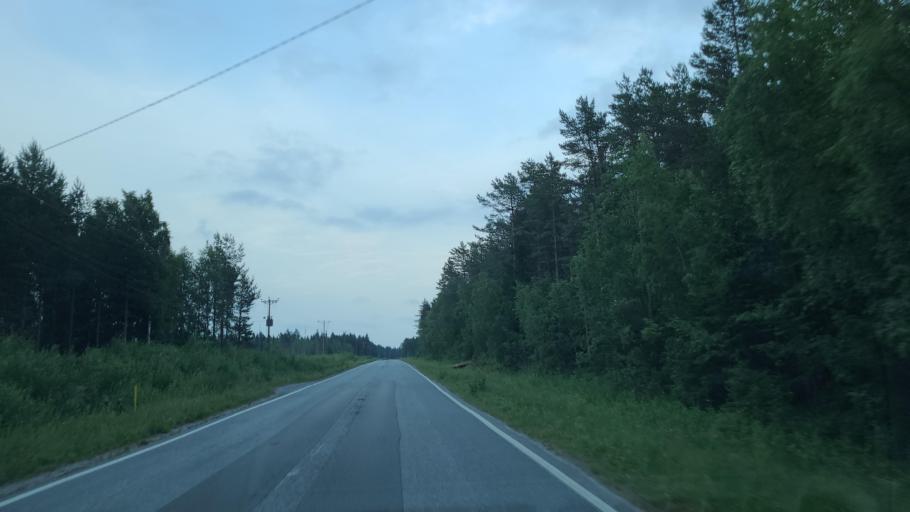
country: FI
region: Ostrobothnia
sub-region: Vaasa
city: Replot
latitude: 63.2026
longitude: 21.2846
